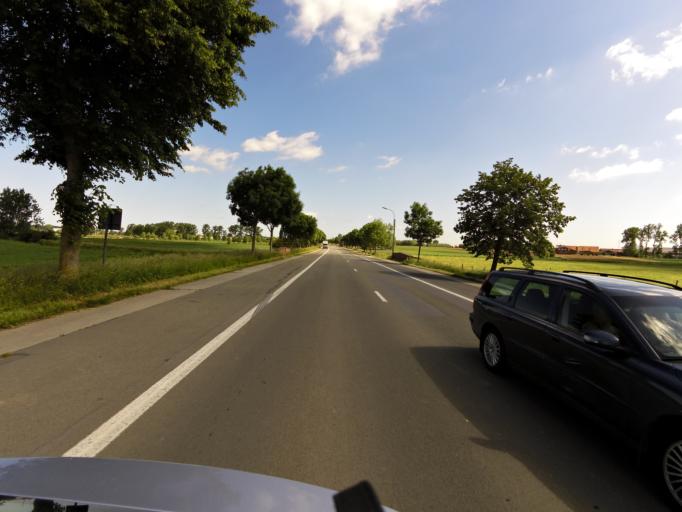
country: BE
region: Flanders
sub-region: Provincie West-Vlaanderen
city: Diksmuide
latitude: 50.9407
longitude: 2.8602
